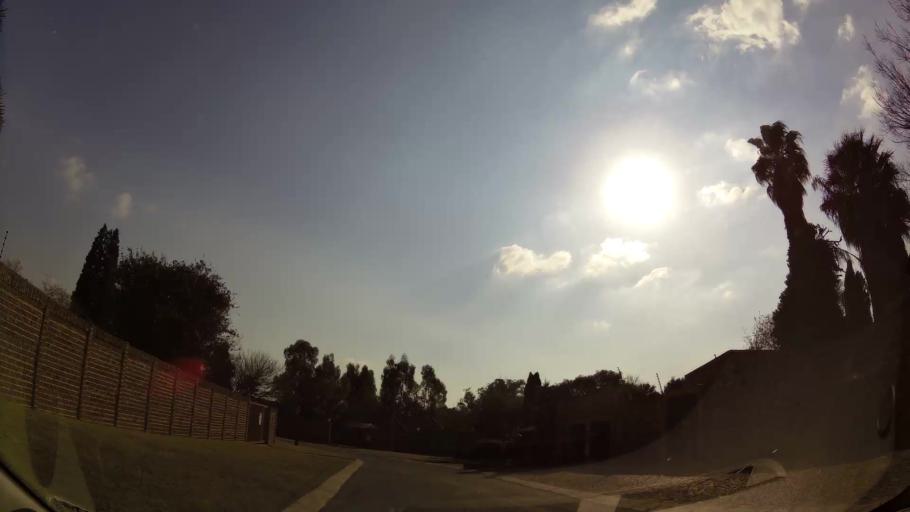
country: ZA
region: Gauteng
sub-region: Ekurhuleni Metropolitan Municipality
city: Benoni
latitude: -26.1460
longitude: 28.2969
